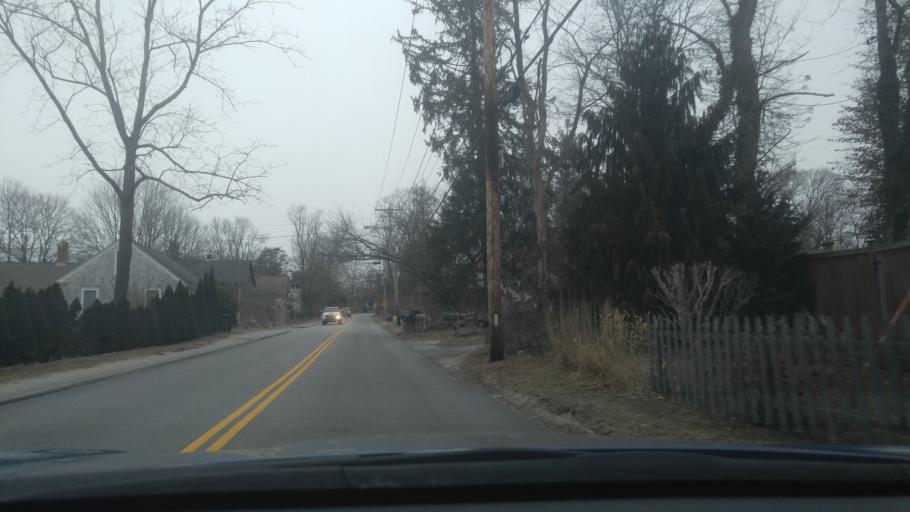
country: US
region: Rhode Island
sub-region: Washington County
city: Wakefield-Peacedale
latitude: 41.4546
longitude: -71.4966
